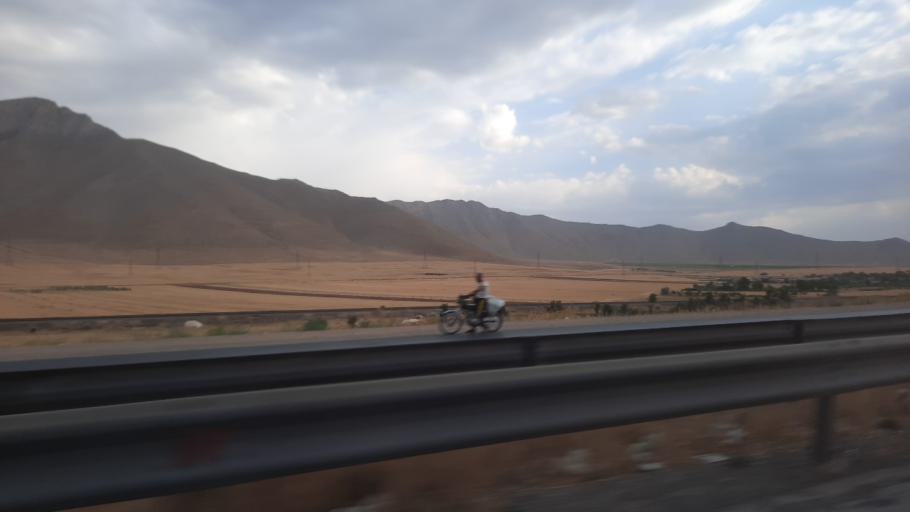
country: IR
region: Markazi
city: Shazand
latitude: 34.0133
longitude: 49.5418
